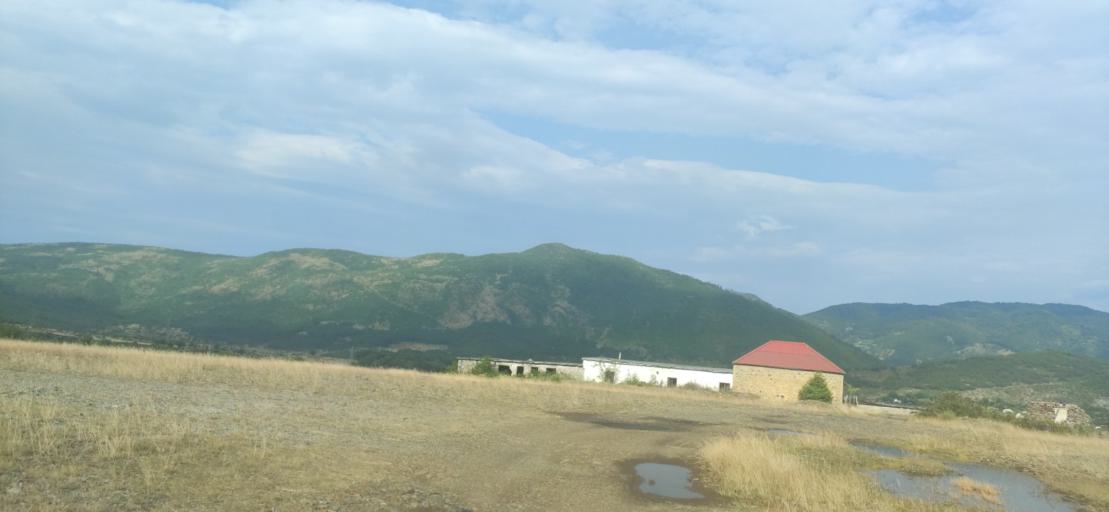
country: AL
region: Shkoder
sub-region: Rrethi i Pukes
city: Iballe
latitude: 42.1872
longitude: 20.0054
